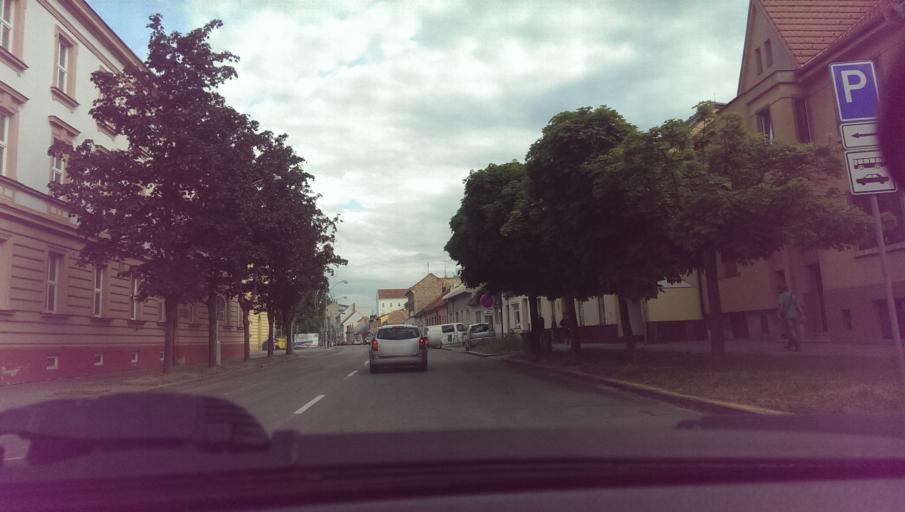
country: CZ
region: Zlin
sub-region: Okres Kromeriz
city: Kromeriz
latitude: 49.2937
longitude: 17.3907
